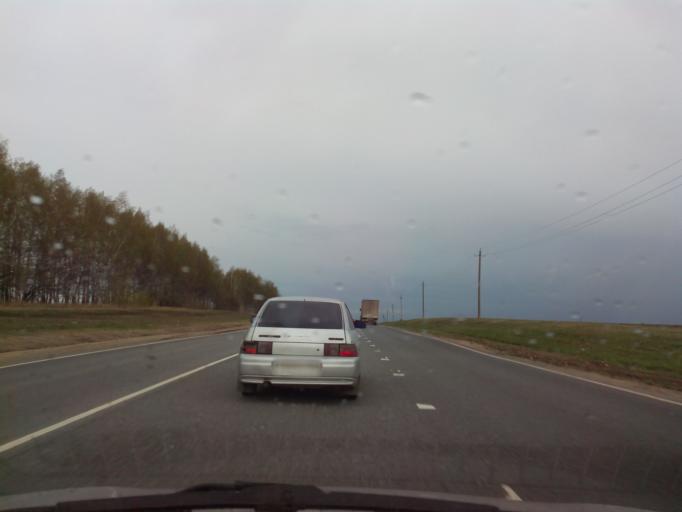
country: RU
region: Moskovskaya
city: Uzunovo
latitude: 54.4952
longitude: 38.5096
